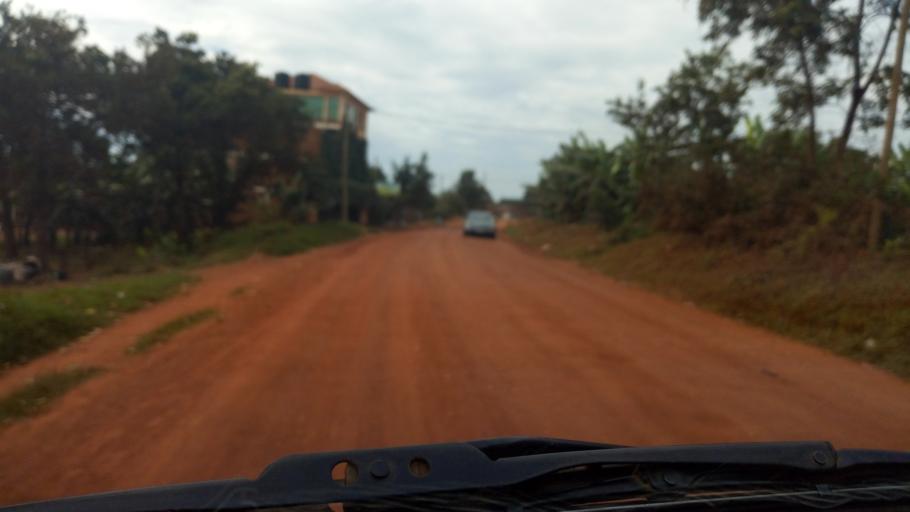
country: UG
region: Central Region
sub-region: Wakiso District
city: Bweyogerere
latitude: 0.3553
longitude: 32.7001
